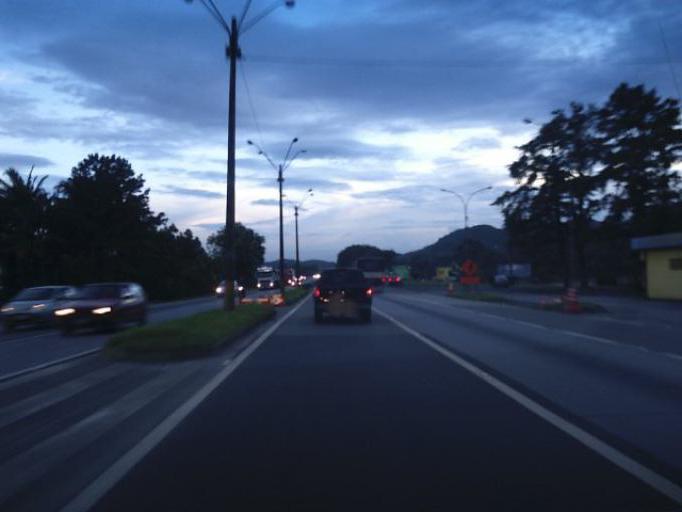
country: BR
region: Santa Catarina
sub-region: Joinville
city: Joinville
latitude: -26.1903
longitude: -48.9119
